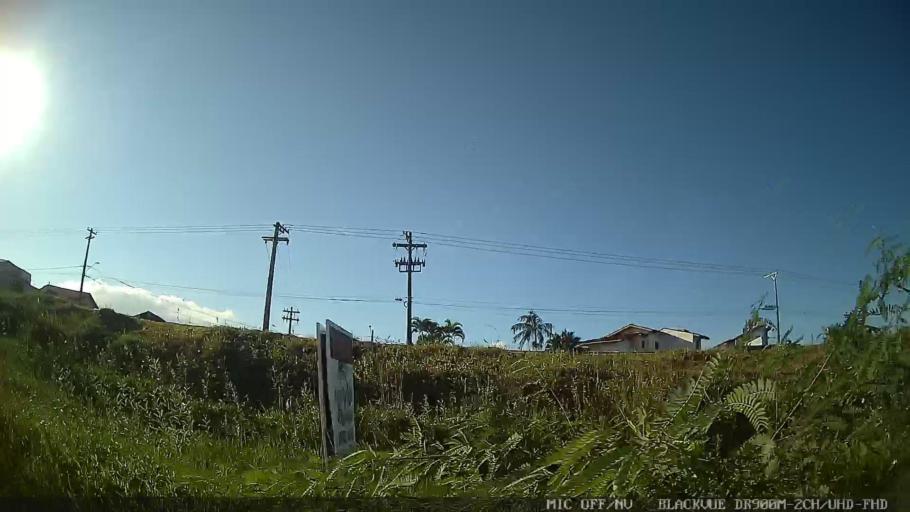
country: BR
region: Sao Paulo
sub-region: Peruibe
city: Peruibe
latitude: -24.2988
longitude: -46.9839
